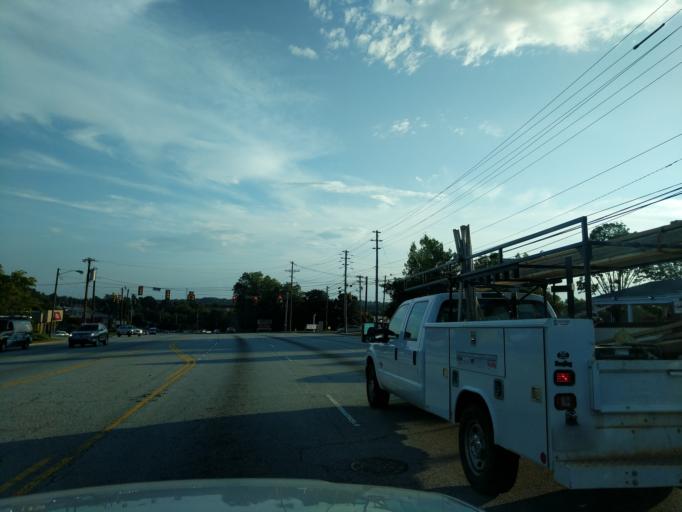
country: US
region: South Carolina
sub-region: Greenville County
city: Greenville
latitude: 34.8311
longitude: -82.3698
